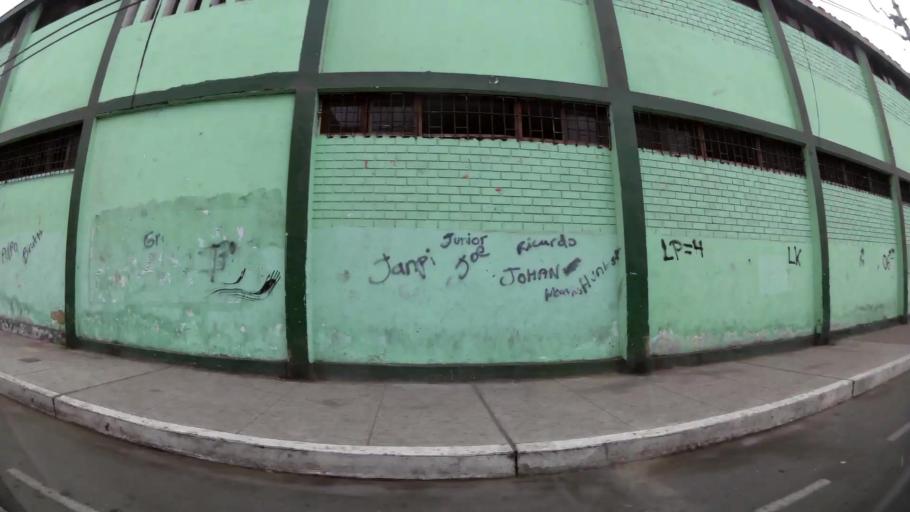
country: PE
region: Callao
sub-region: Callao
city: Callao
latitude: -12.0624
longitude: -77.1353
